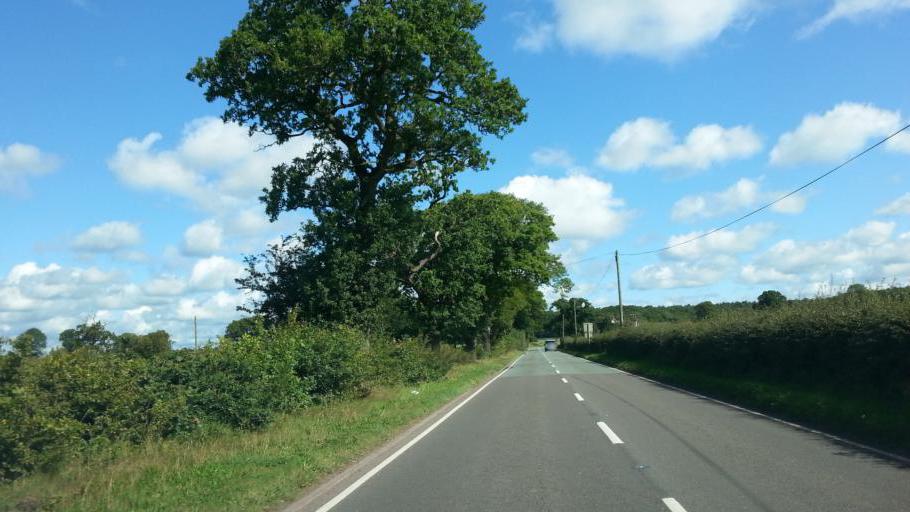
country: GB
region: England
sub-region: Staffordshire
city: Uttoxeter
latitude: 52.8296
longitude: -1.8997
